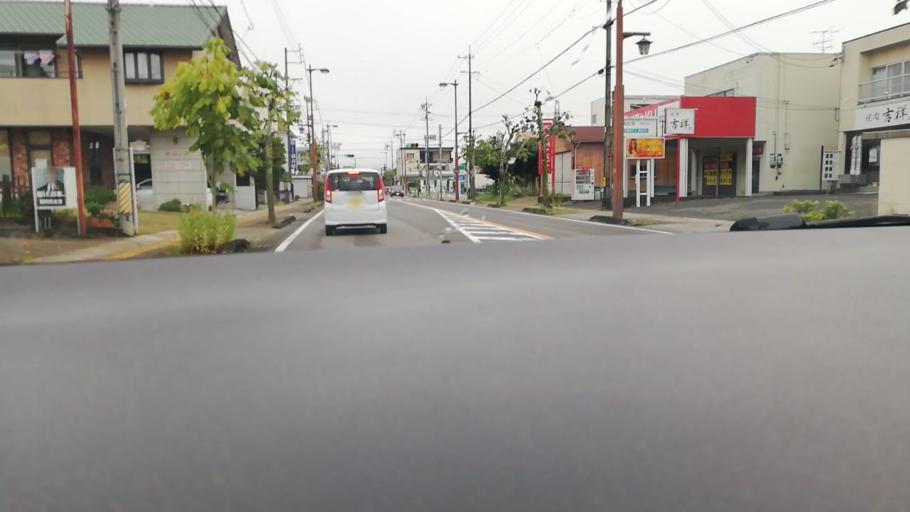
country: JP
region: Aichi
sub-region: Toyota-shi
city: Toyota
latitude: 35.0916
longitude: 137.1834
